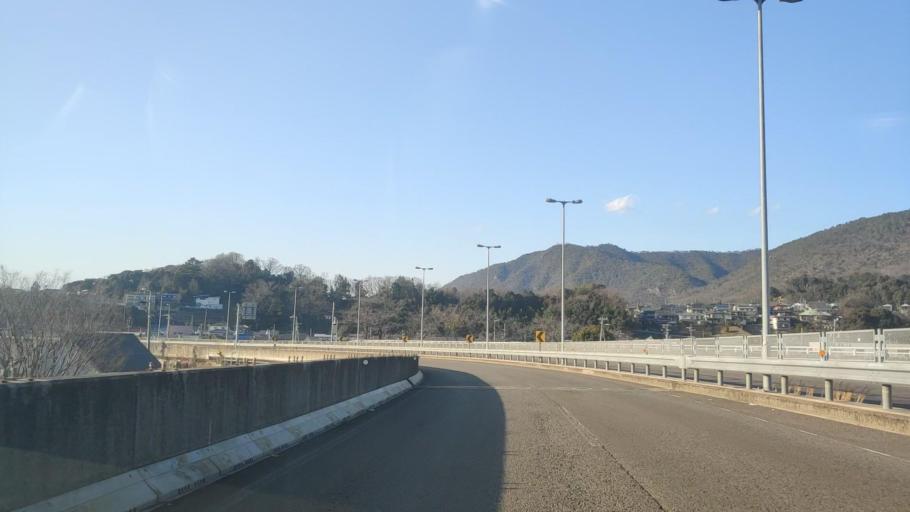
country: JP
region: Gifu
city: Gifu-shi
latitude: 35.4426
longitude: 136.7945
